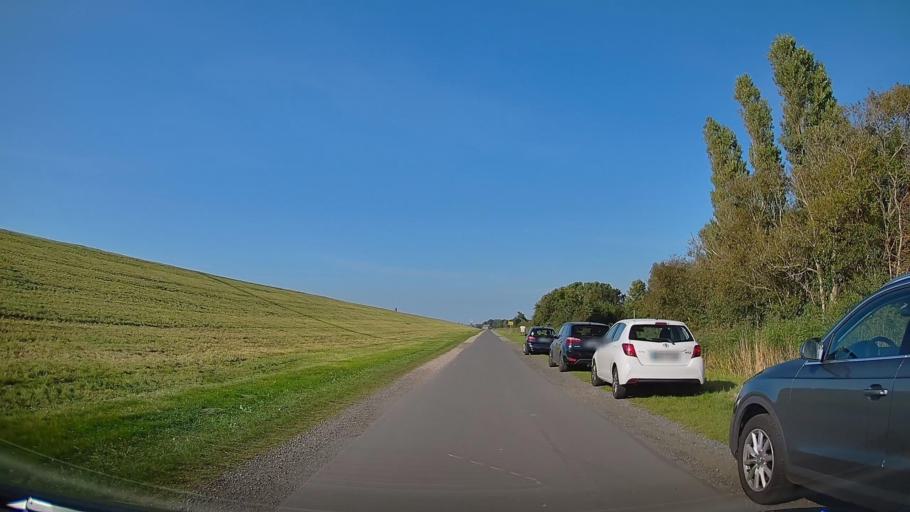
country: DE
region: Lower Saxony
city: Wremen
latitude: 53.6495
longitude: 8.4952
